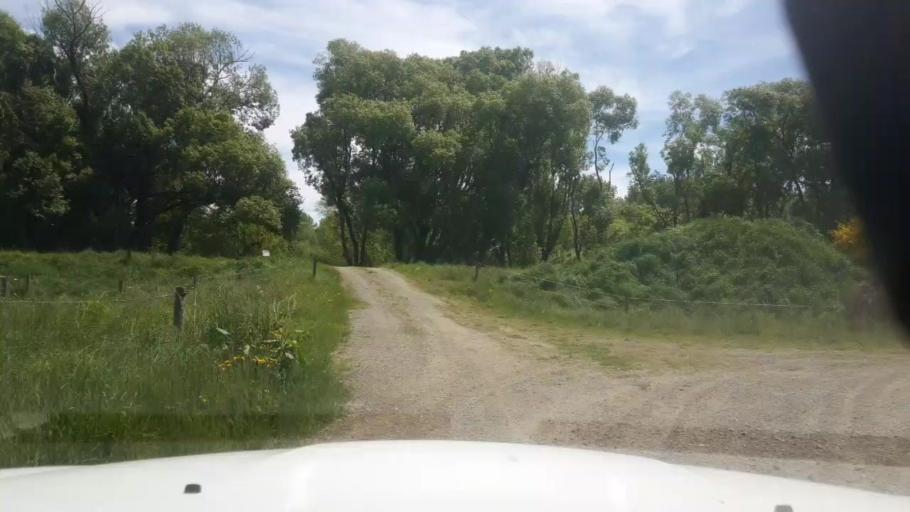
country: NZ
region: Canterbury
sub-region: Timaru District
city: Pleasant Point
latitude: -44.2573
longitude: 171.0905
